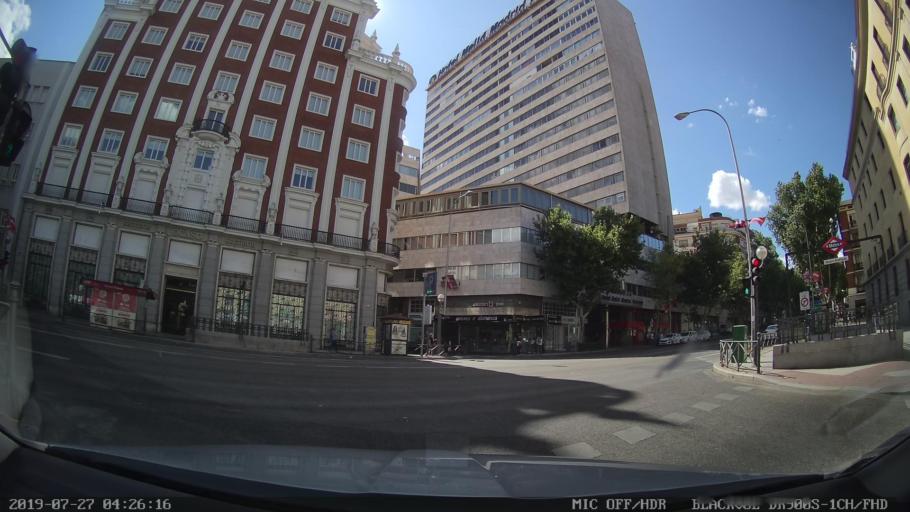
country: ES
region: Madrid
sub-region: Provincia de Madrid
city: Chamberi
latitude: 40.4266
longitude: -3.7115
